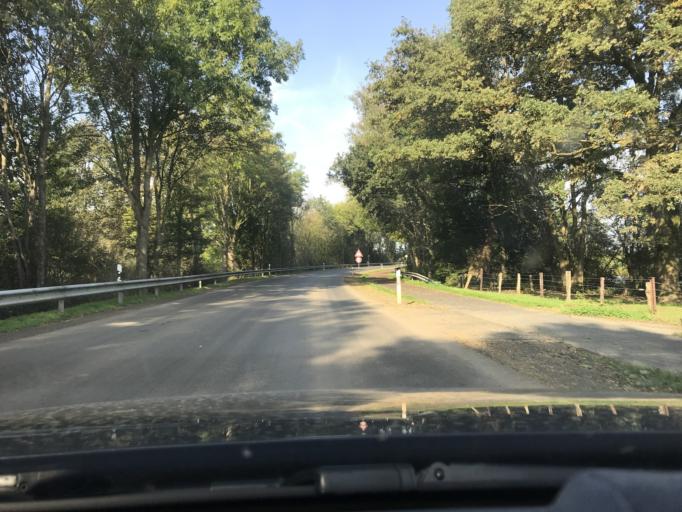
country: DE
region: North Rhine-Westphalia
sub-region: Regierungsbezirk Dusseldorf
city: Emmerich
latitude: 51.7822
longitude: 6.2307
